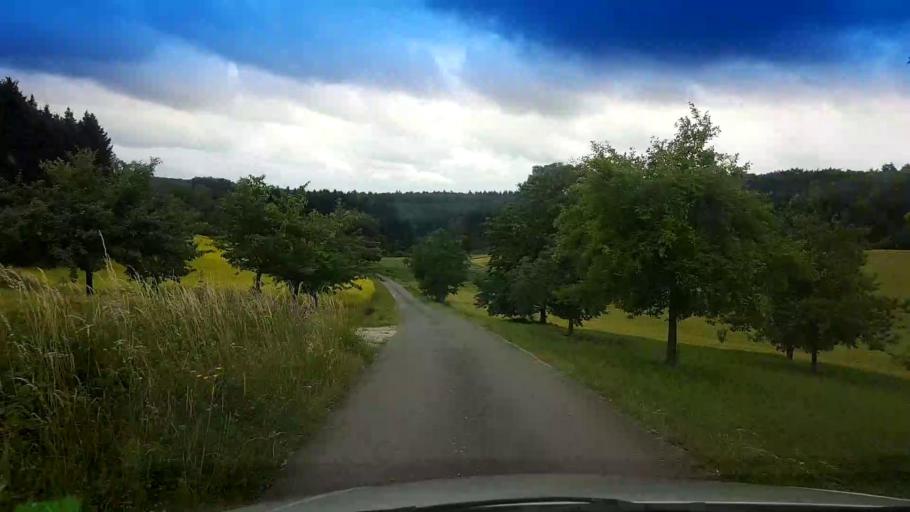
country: DE
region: Bavaria
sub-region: Upper Franconia
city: Poxdorf
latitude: 49.8959
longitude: 11.0807
